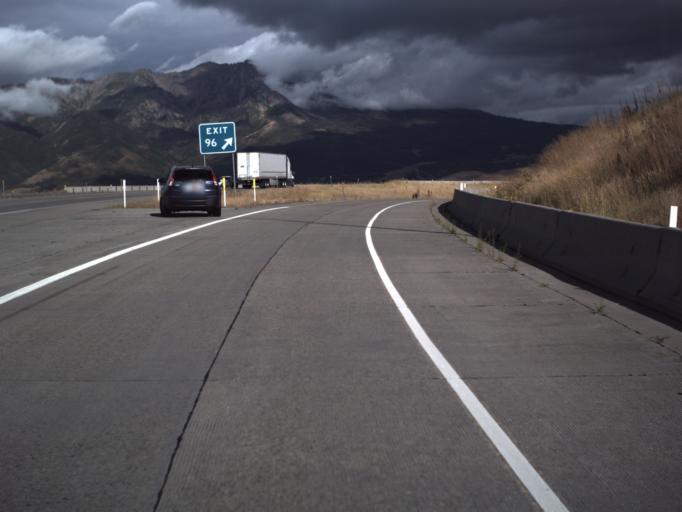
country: US
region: Utah
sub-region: Morgan County
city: Mountain Green
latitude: 41.1132
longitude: -111.7613
